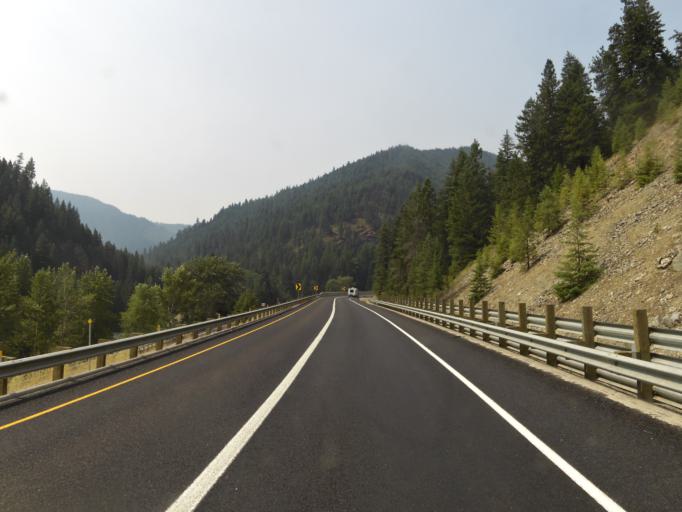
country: US
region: Montana
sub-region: Sanders County
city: Thompson Falls
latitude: 47.3135
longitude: -115.2299
